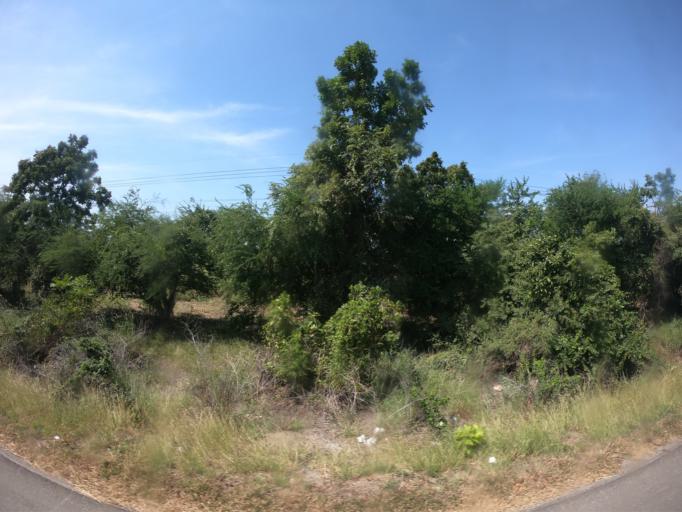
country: TH
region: Nakhon Ratchasima
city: Bua Lai
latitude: 15.6574
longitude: 102.5727
